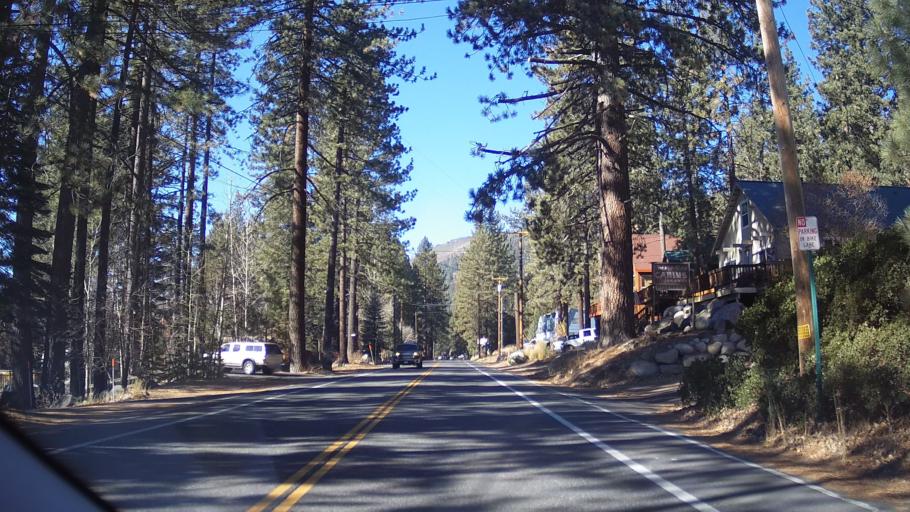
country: US
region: California
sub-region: Nevada County
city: Truckee
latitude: 39.3278
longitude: -120.2442
